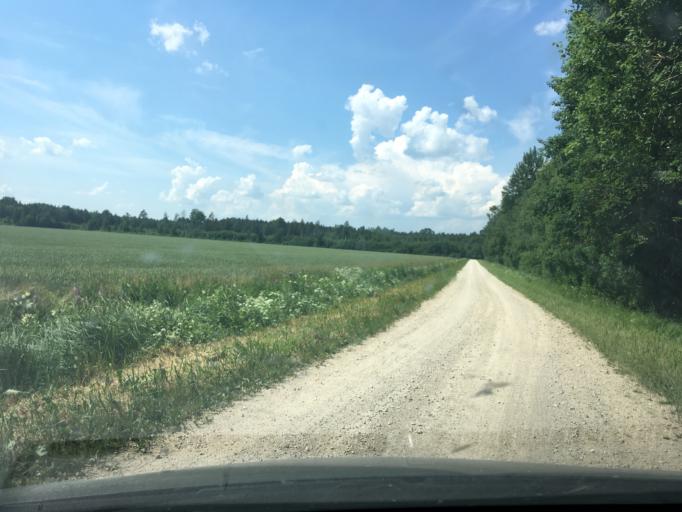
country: EE
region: Raplamaa
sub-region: Maerjamaa vald
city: Marjamaa
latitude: 58.7966
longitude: 24.4592
